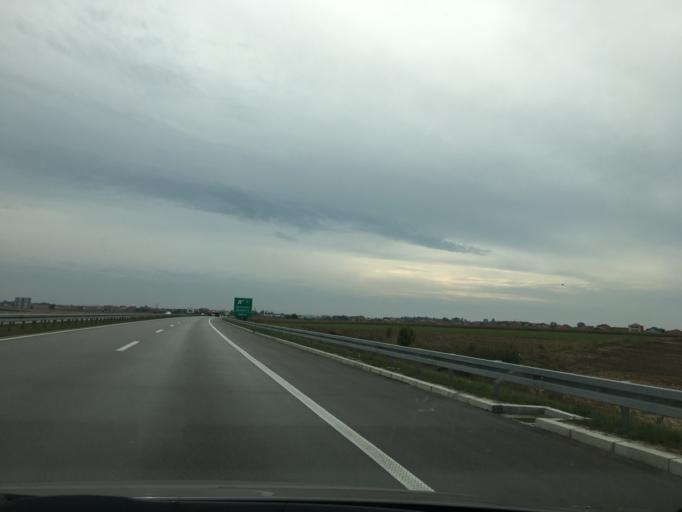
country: RS
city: Novi Banovci
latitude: 44.9093
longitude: 20.3051
